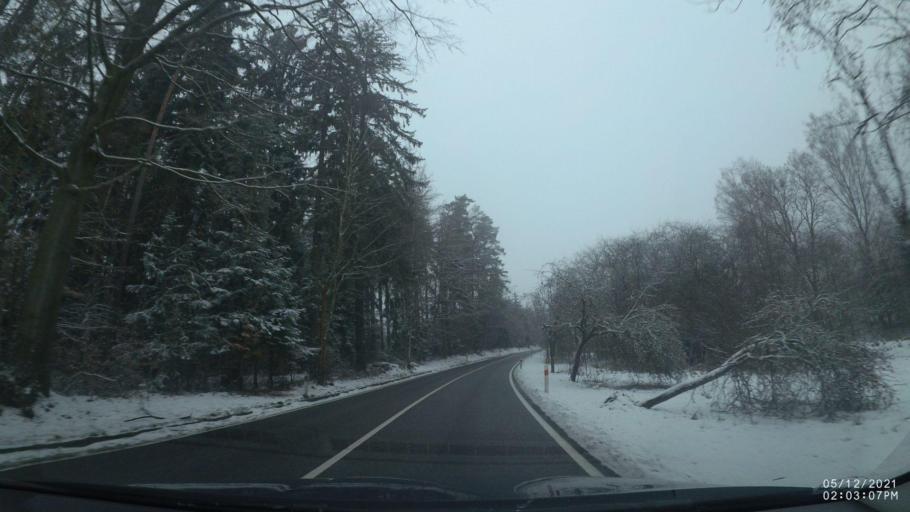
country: CZ
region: Kralovehradecky
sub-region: Okres Nachod
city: Cerveny Kostelec
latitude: 50.4879
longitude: 16.1342
